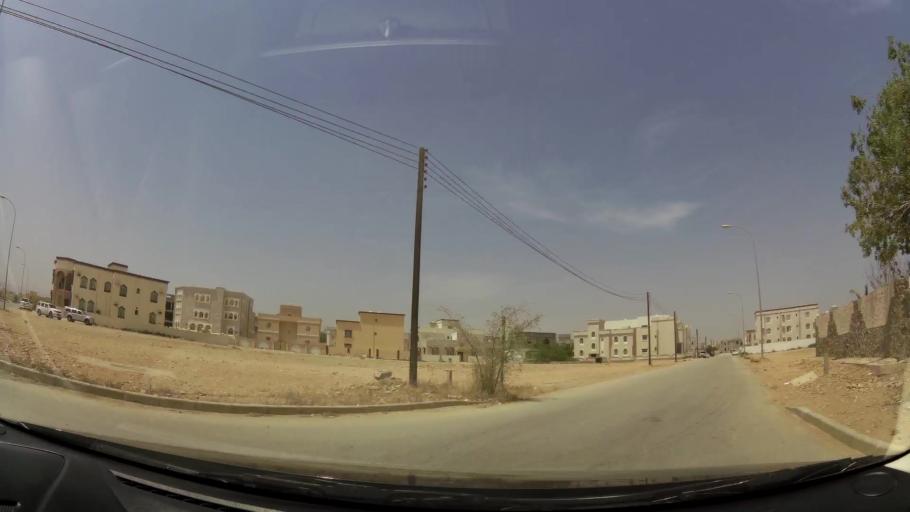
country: OM
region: Zufar
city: Salalah
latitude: 17.0603
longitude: 54.1573
